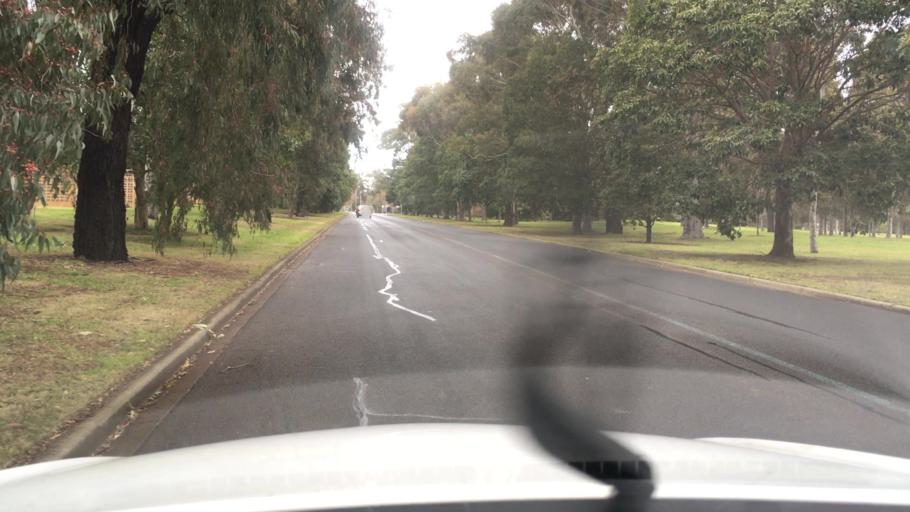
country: AU
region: Victoria
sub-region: Greater Dandenong
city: Noble Park North
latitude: -37.9421
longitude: 145.1775
